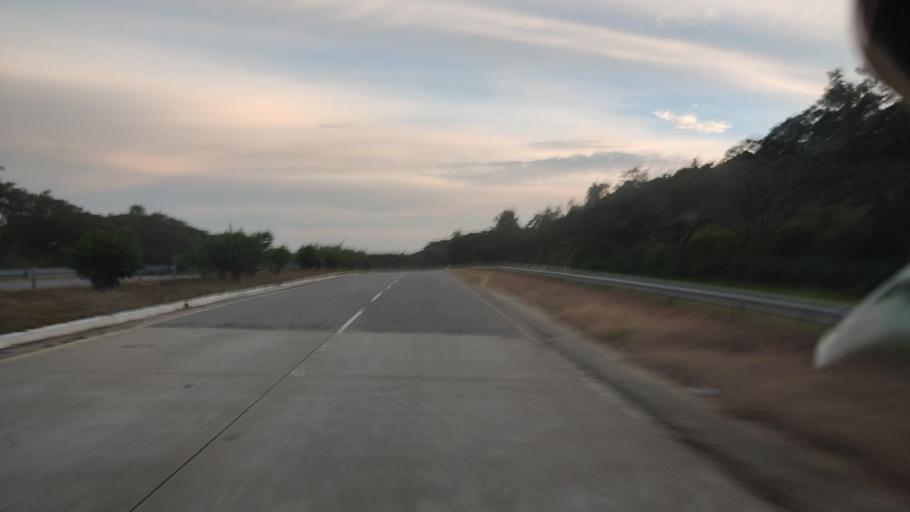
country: MM
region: Mandalay
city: Yamethin
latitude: 20.2640
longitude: 95.8903
